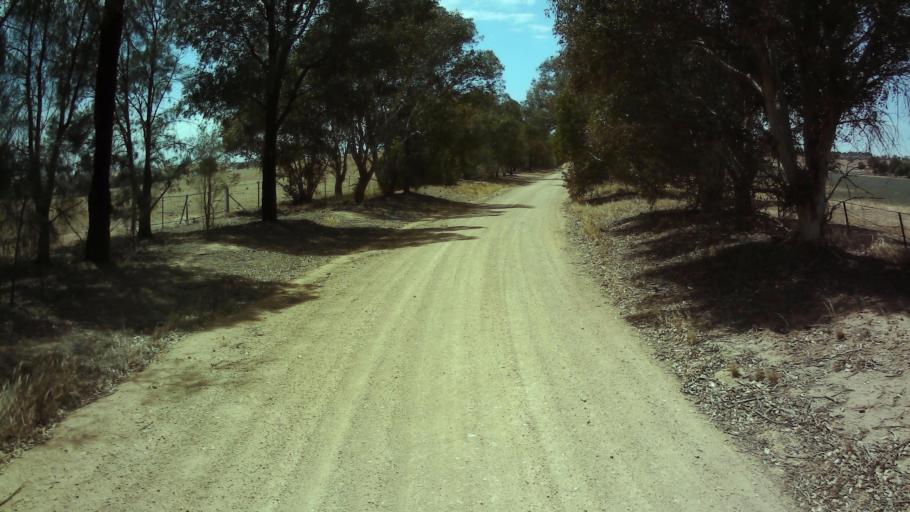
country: AU
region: New South Wales
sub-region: Cowra
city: Cowra
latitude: -33.9579
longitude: 148.4479
